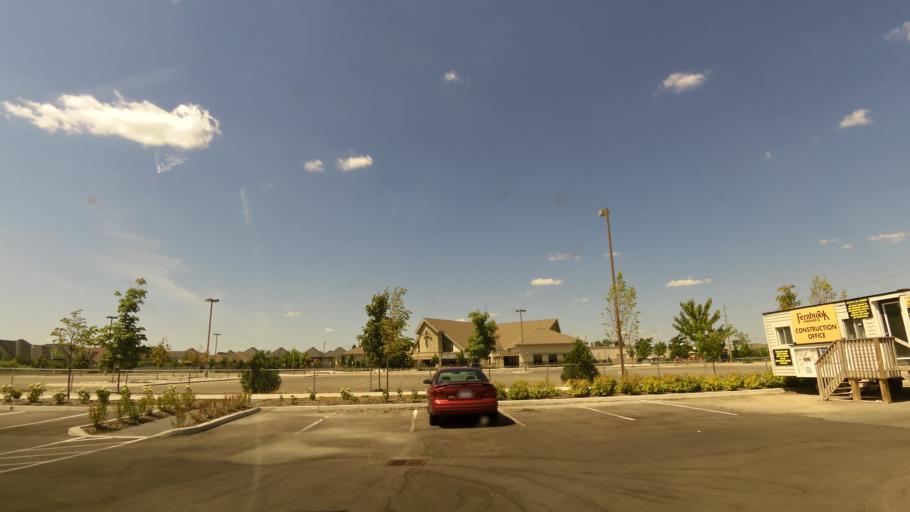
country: CA
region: Ontario
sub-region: Halton
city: Milton
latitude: 43.6301
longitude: -79.8775
